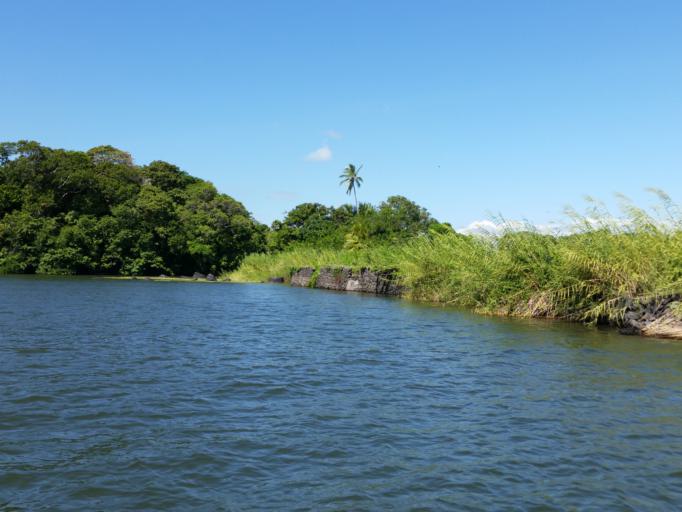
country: NI
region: Granada
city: Granada
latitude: 11.8841
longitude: -85.8927
